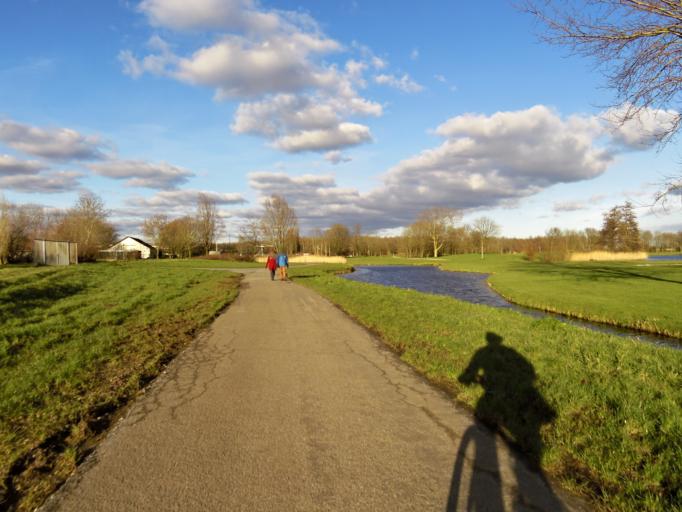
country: NL
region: South Holland
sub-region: Gemeente Leiden
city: Leiden
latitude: 52.1849
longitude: 4.5013
